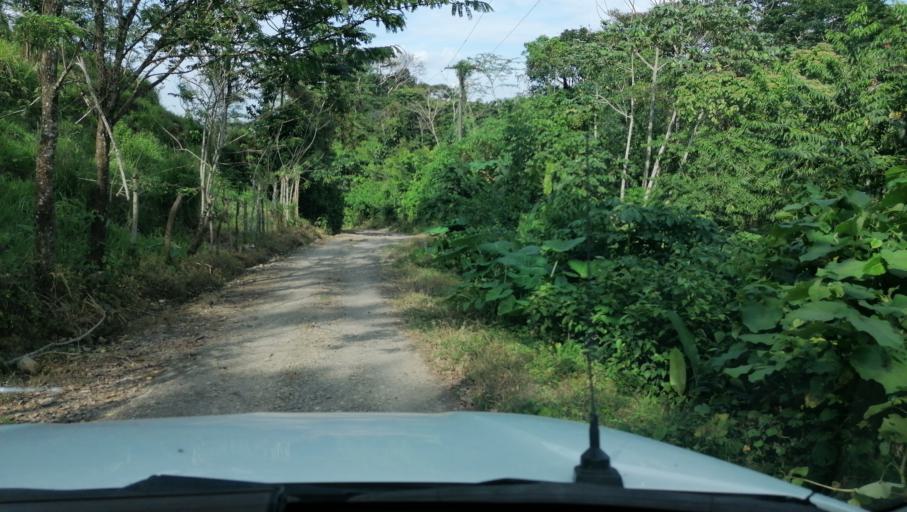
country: MX
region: Chiapas
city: Ostuacan
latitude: 17.4547
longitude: -93.2426
